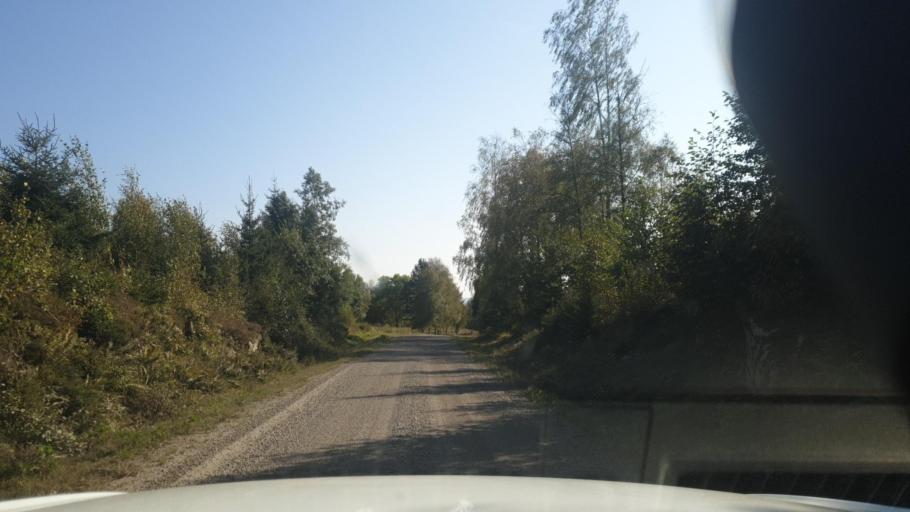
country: SE
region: Vaermland
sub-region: Eda Kommun
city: Charlottenberg
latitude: 59.9976
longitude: 12.5084
